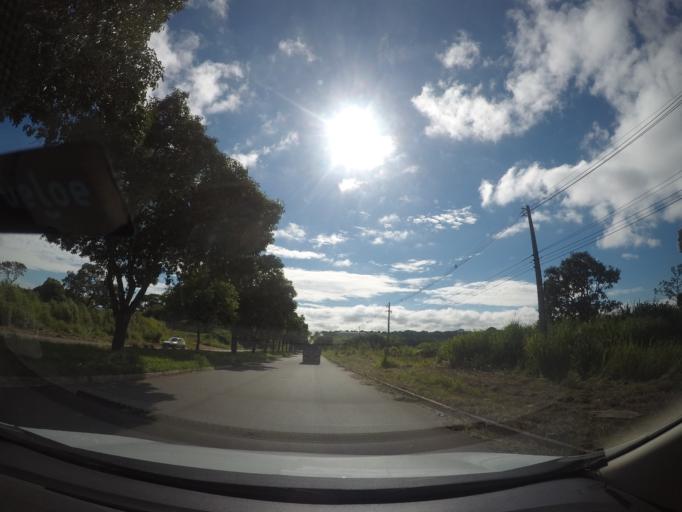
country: BR
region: Goias
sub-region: Goiania
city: Goiania
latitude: -16.6519
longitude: -49.1708
